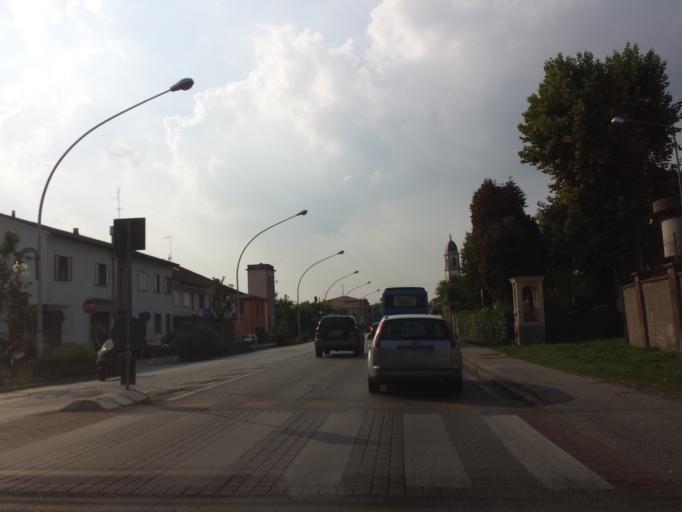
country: IT
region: Veneto
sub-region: Provincia di Padova
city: Caselle
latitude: 45.4131
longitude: 11.8393
